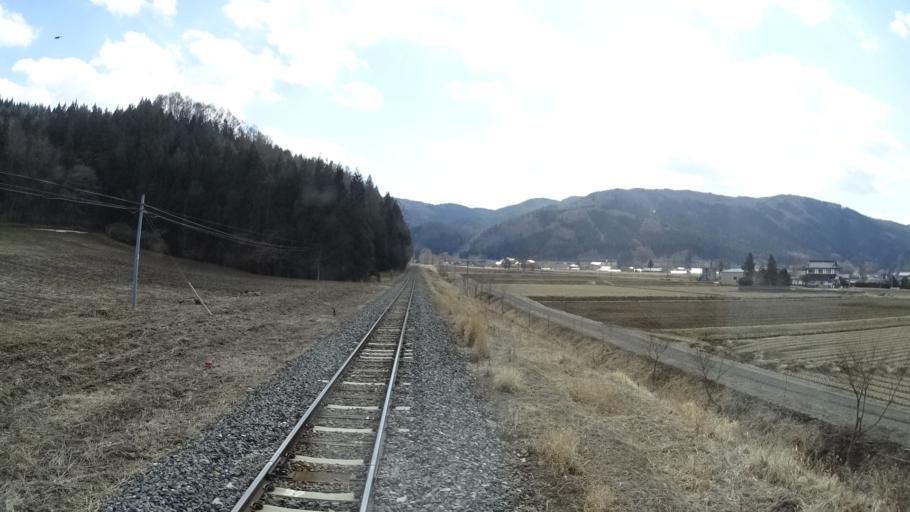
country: JP
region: Iwate
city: Tono
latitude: 39.2738
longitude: 141.5901
